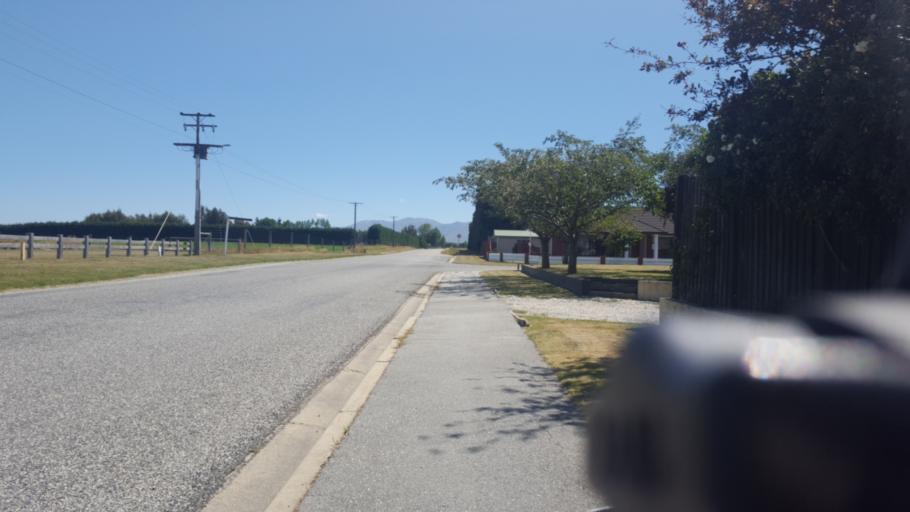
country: NZ
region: Otago
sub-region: Dunedin City
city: Dunedin
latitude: -45.1252
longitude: 170.1062
